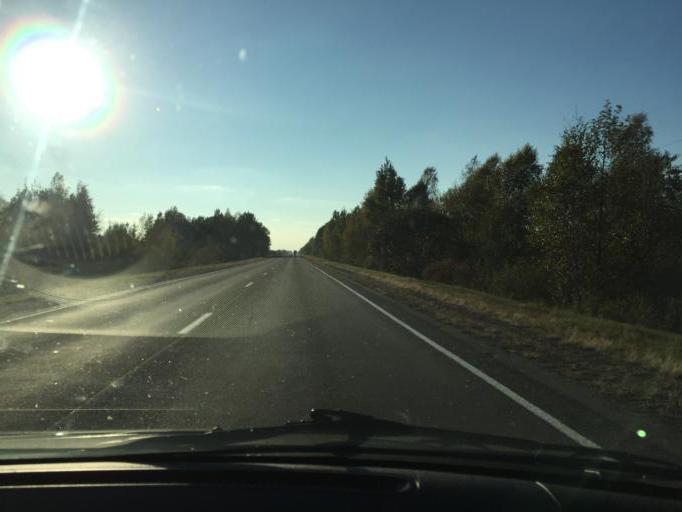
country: BY
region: Brest
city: Horad Luninyets
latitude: 52.3120
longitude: 26.5427
